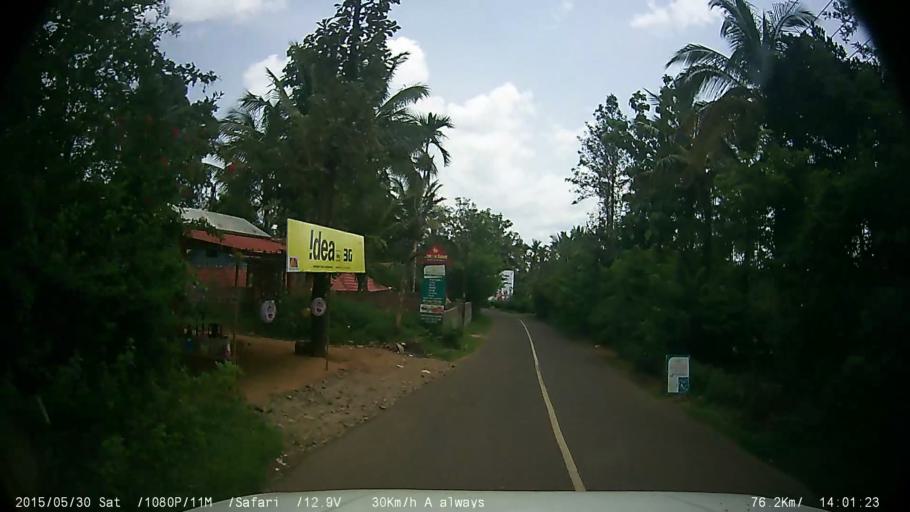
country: IN
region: Kerala
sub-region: Wayanad
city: Panamaram
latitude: 11.8236
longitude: 76.0632
